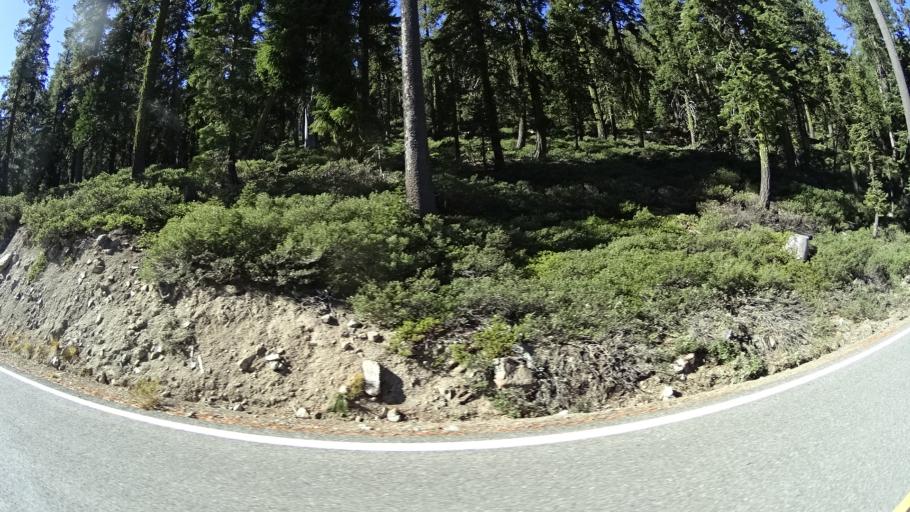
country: US
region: California
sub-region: Trinity County
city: Weaverville
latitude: 41.2312
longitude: -122.8969
